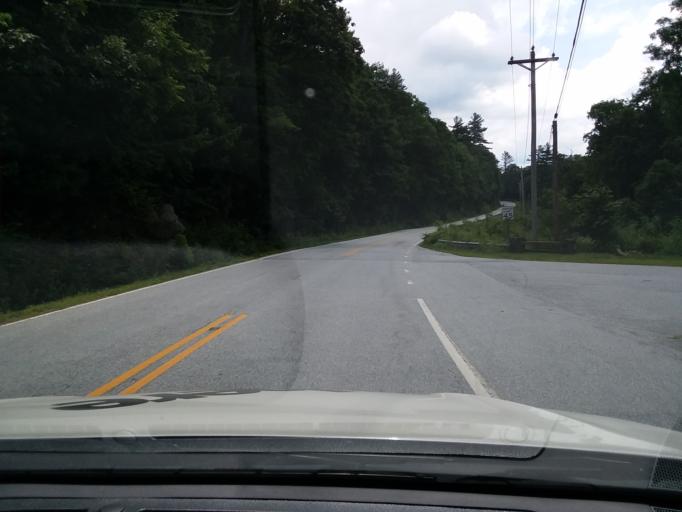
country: US
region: Georgia
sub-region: Rabun County
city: Mountain City
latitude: 35.0291
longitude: -83.2819
